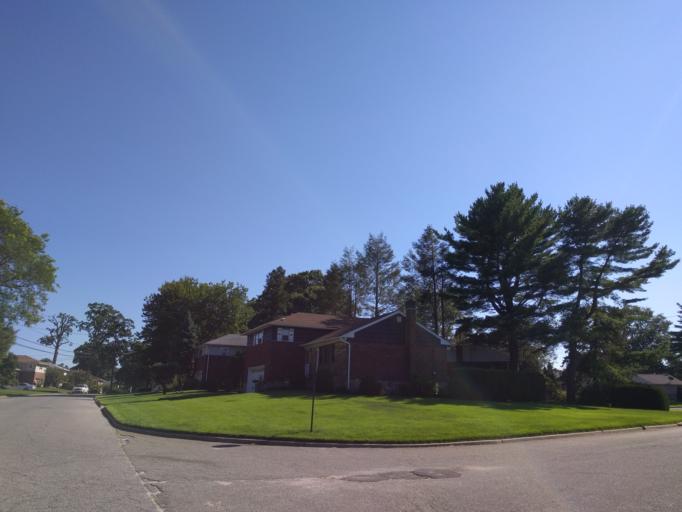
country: US
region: New York
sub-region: Nassau County
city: Locust Valley
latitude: 40.8769
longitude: -73.6165
